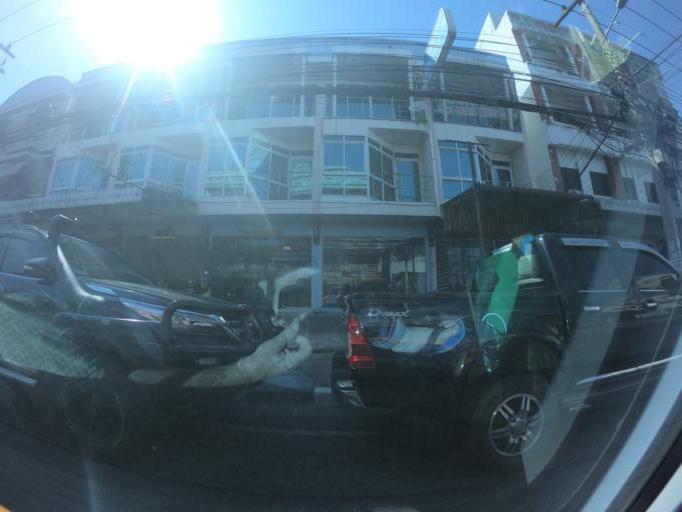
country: TH
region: Khon Kaen
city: Khon Kaen
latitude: 16.4157
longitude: 102.8341
